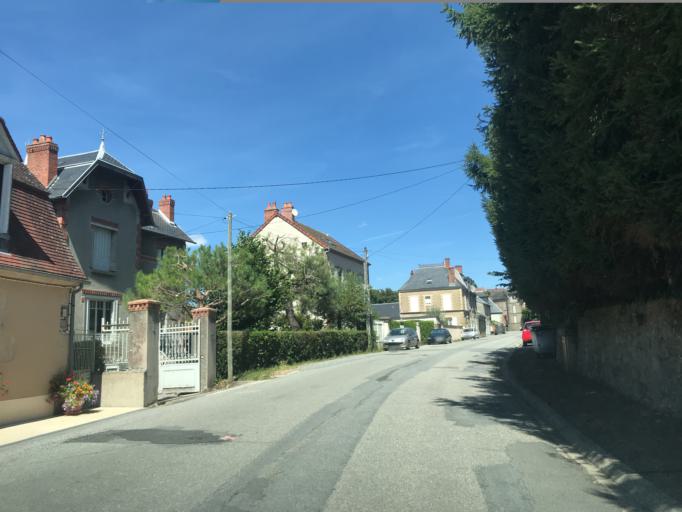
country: FR
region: Limousin
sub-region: Departement de la Creuse
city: Felletin
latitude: 45.8788
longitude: 2.1724
